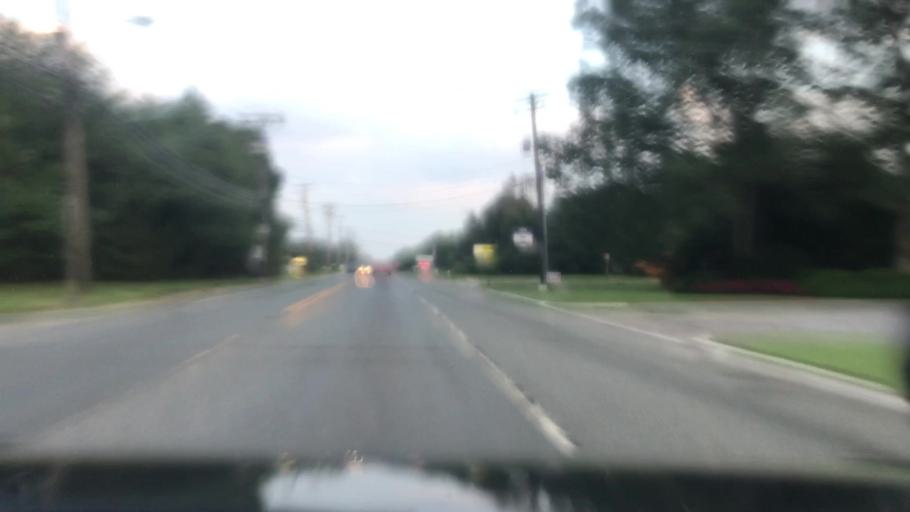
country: US
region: New Jersey
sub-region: Ocean County
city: Pine Lake Park
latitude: 40.0161
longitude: -74.2187
